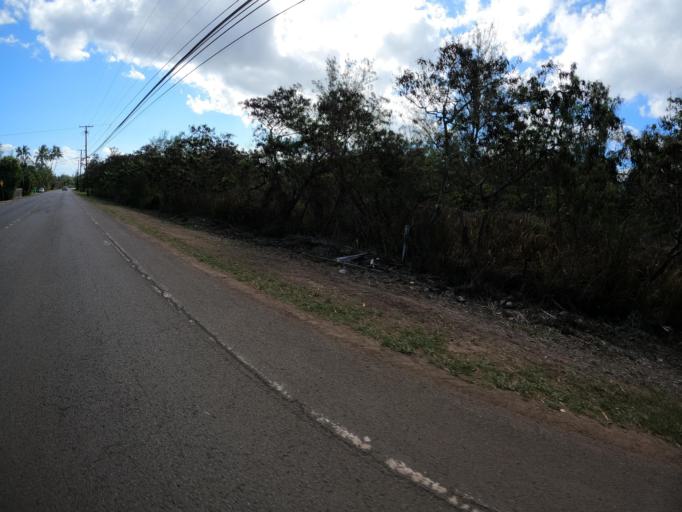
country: US
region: Hawaii
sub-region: Honolulu County
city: Mokuleia
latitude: 21.5793
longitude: -158.1763
